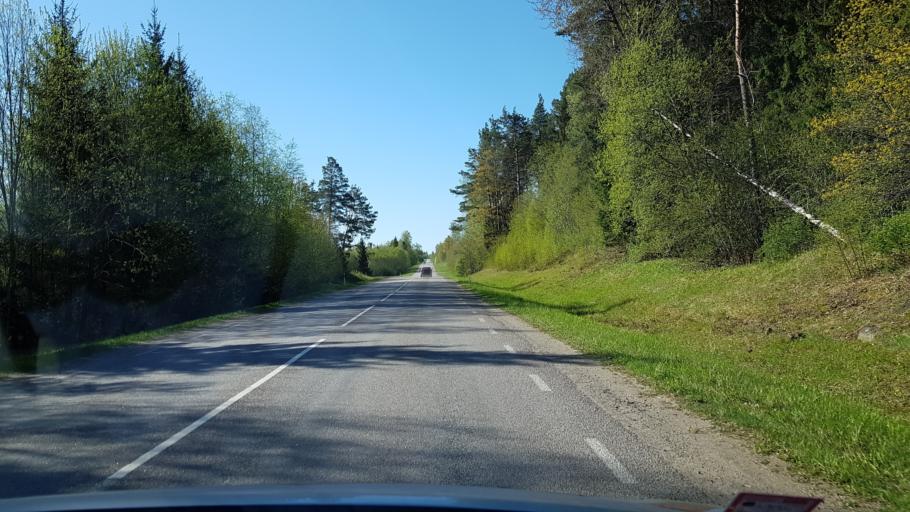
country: EE
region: Vorumaa
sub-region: Voru linn
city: Voru
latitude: 57.7929
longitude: 27.0342
